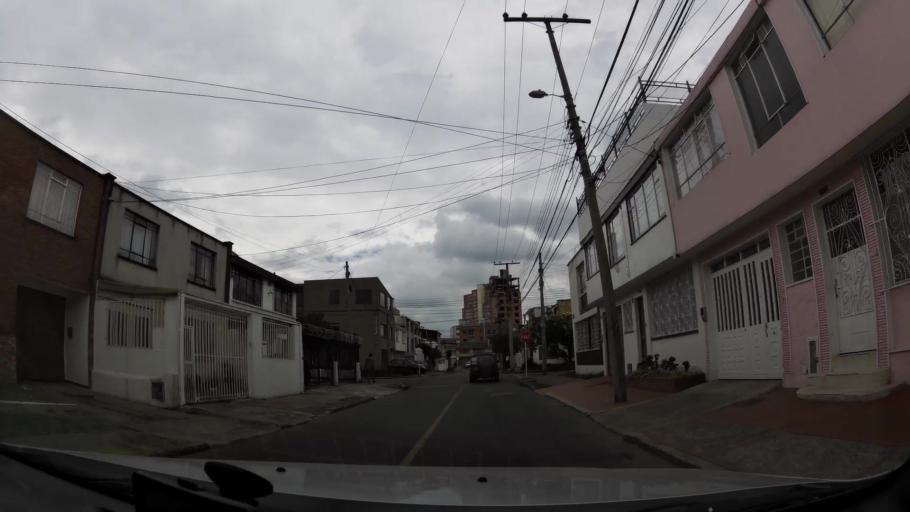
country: CO
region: Bogota D.C.
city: Bogota
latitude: 4.6312
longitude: -74.0879
